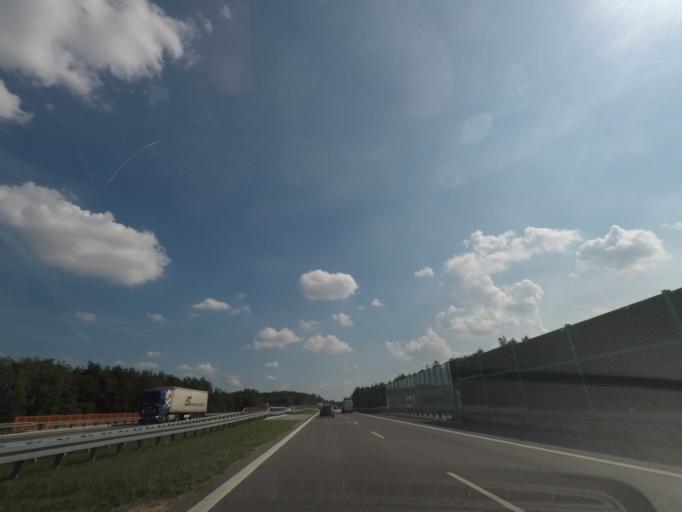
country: PL
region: Lodz Voivodeship
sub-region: Powiat lodzki wschodni
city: Tuszyn
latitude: 51.5676
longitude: 19.6000
